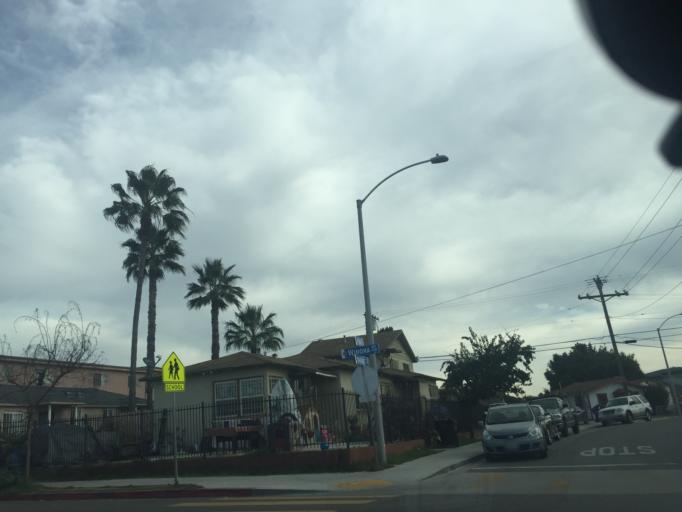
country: US
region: California
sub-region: San Diego County
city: Lemon Grove
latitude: 32.7514
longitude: -117.0880
